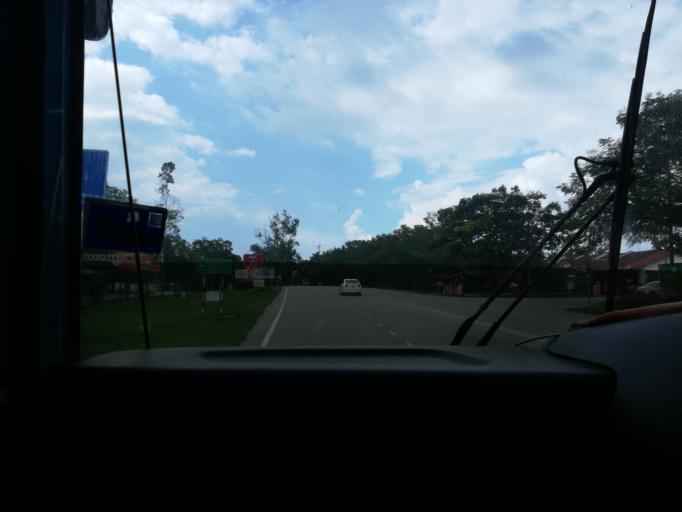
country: MY
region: Kedah
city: Kulim
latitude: 5.3698
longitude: 100.5813
